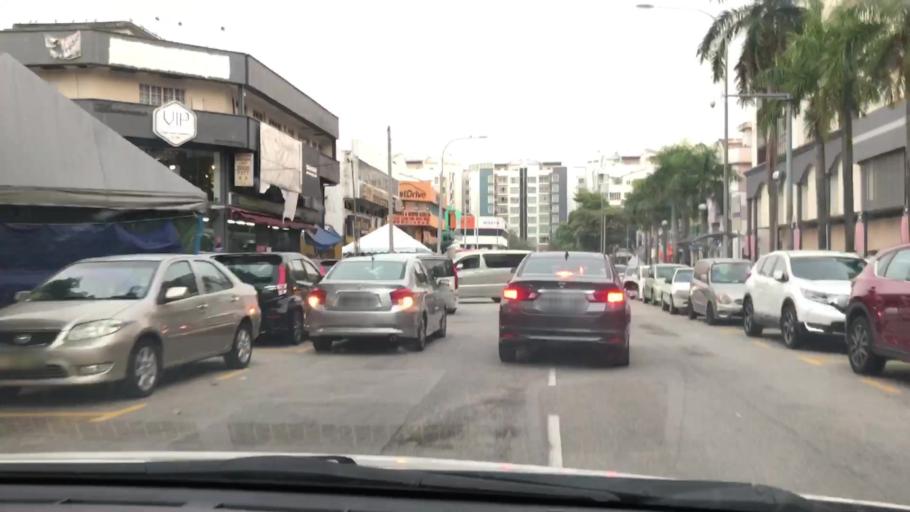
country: MY
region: Selangor
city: Kampong Baharu Balakong
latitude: 3.0688
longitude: 101.6904
